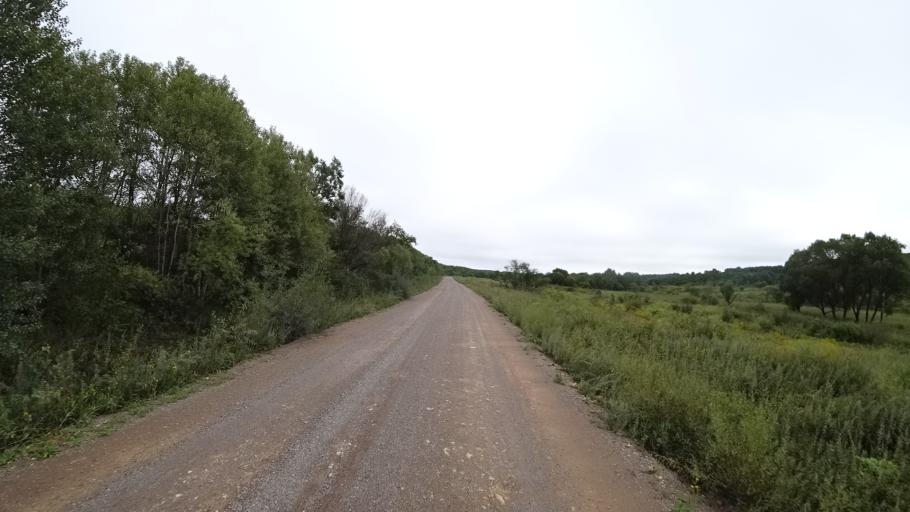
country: RU
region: Primorskiy
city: Ivanovka
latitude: 44.0510
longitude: 132.4865
